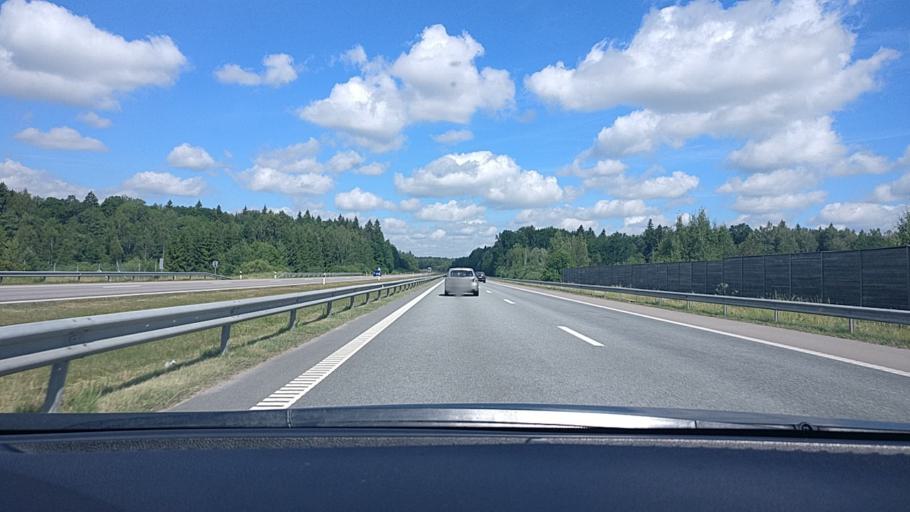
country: LT
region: Vilnius County
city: Pasilaiciai
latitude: 54.8361
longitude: 25.1190
